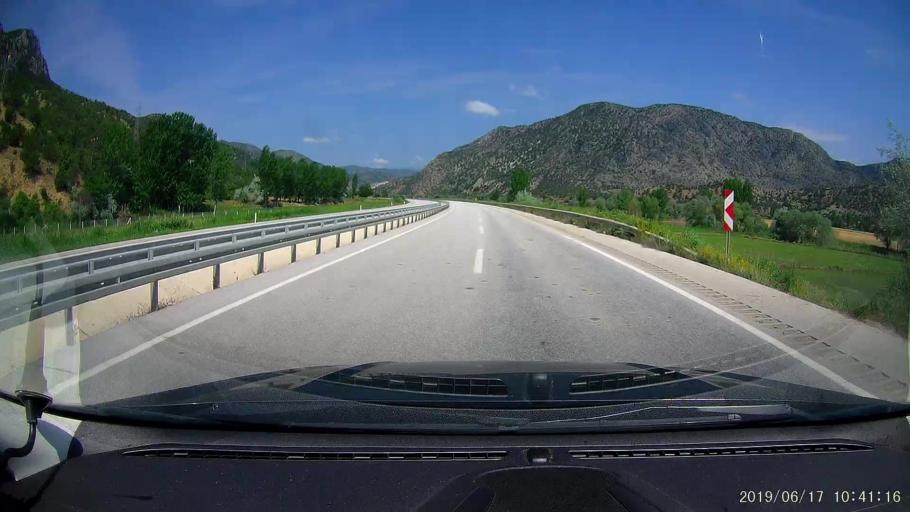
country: TR
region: Corum
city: Kargi
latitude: 41.0376
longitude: 34.5808
